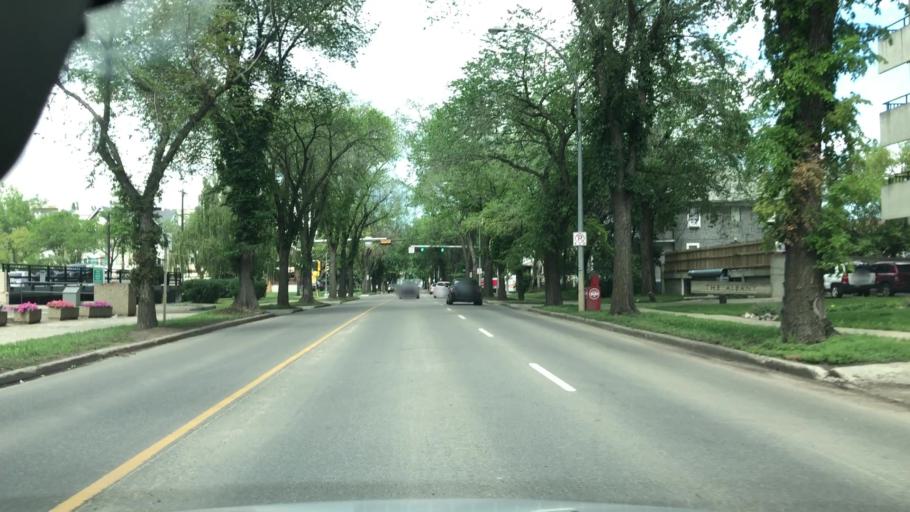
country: CA
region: Alberta
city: Edmonton
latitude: 53.5420
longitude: -113.5213
